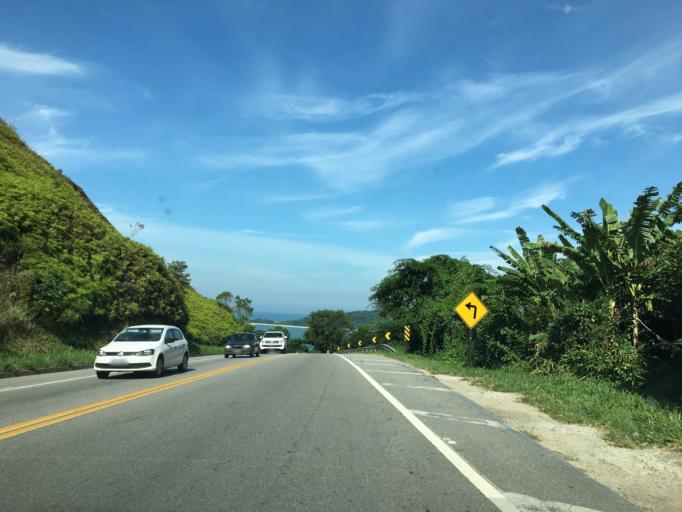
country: BR
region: Sao Paulo
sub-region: Sao Sebastiao
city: Sao Sebastiao
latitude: -23.7711
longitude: -45.7204
